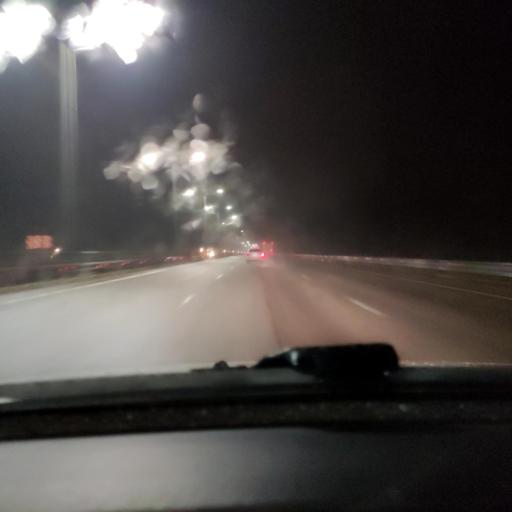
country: RU
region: Voronezj
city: Somovo
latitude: 51.7073
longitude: 39.3066
